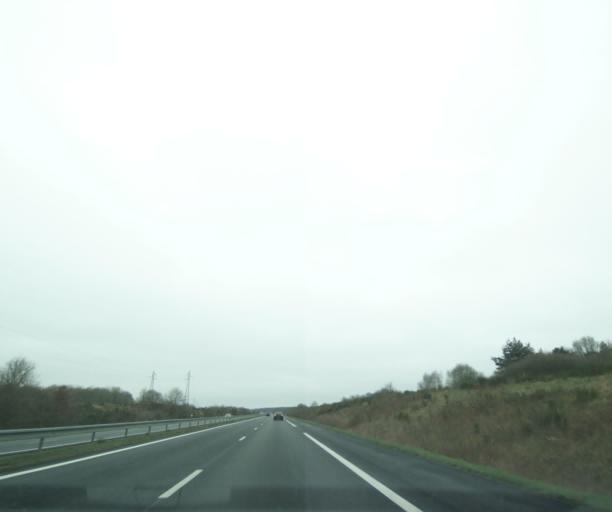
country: FR
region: Centre
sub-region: Departement du Loir-et-Cher
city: Theillay
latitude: 47.3056
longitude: 2.0443
